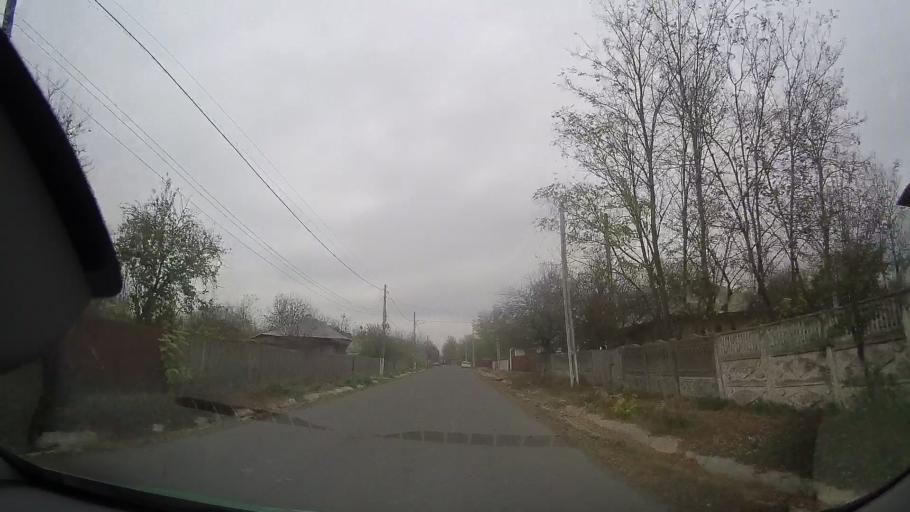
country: RO
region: Braila
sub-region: Comuna Ciocile
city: Ciocile
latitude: 44.8067
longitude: 27.2741
